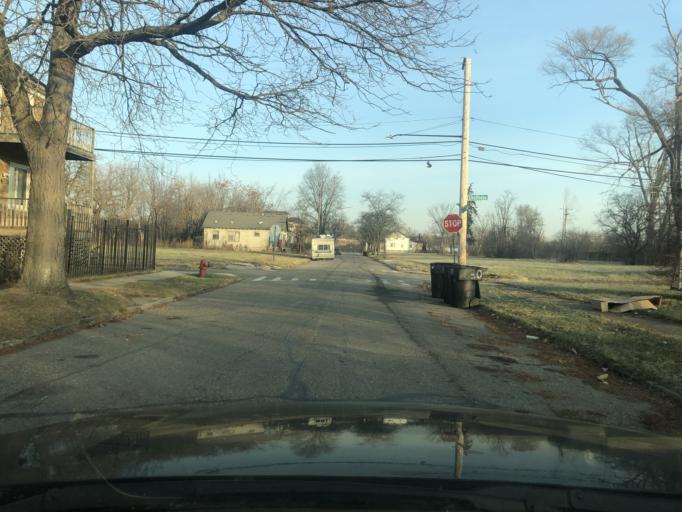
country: US
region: Michigan
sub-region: Wayne County
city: Highland Park
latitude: 42.4005
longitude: -83.1308
